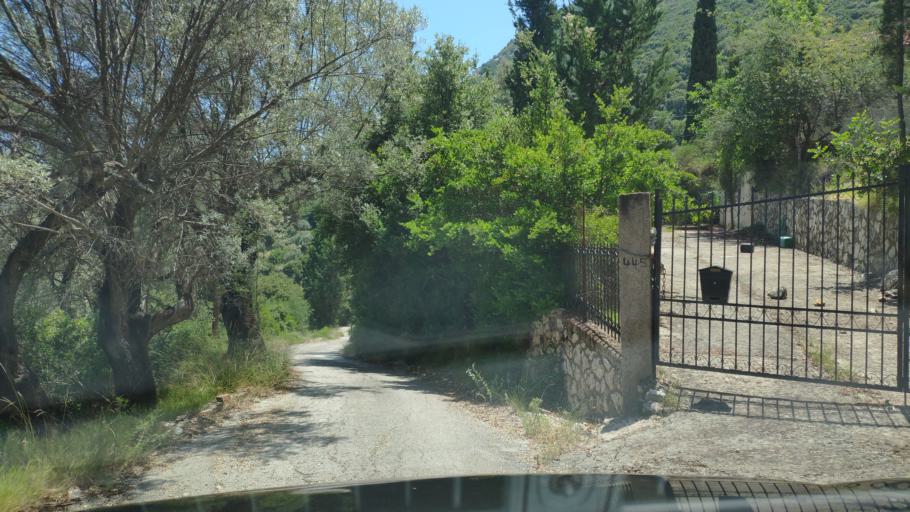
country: GR
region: Ionian Islands
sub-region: Lefkada
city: Nidri
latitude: 38.7533
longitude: 20.7140
